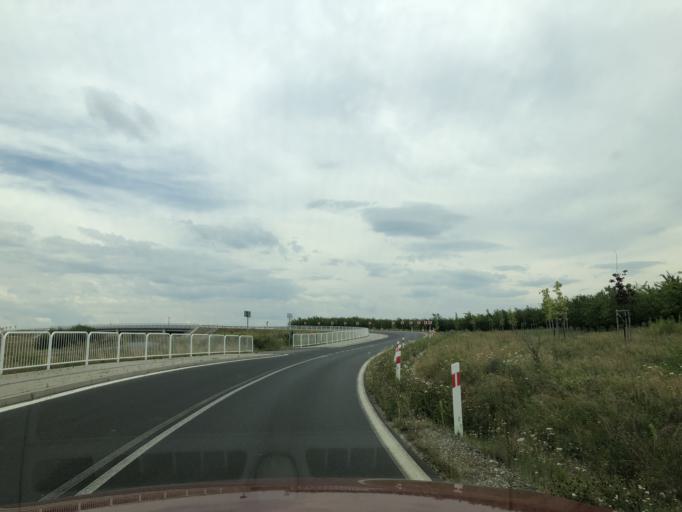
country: PL
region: Lower Silesian Voivodeship
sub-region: Powiat trzebnicki
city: Trzebnica
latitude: 51.3197
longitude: 17.0336
